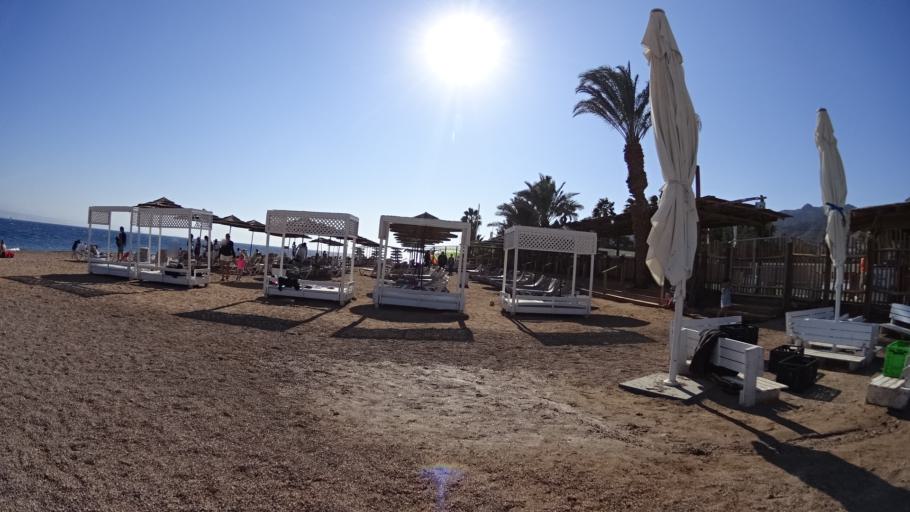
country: IL
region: Southern District
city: Eilat
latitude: 29.5132
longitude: 34.9260
